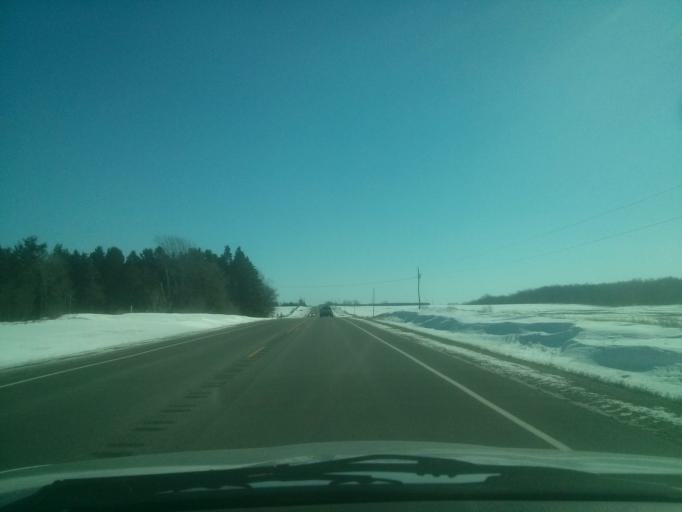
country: US
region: Wisconsin
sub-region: Polk County
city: Clear Lake
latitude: 45.1363
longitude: -92.3146
